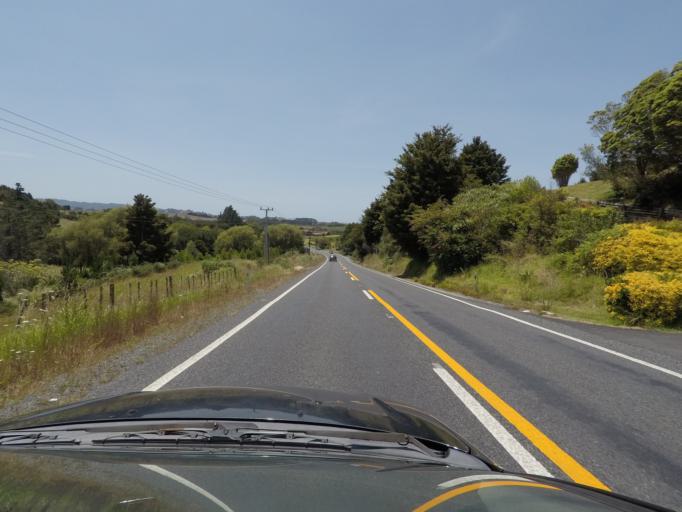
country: NZ
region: Auckland
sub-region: Auckland
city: Warkworth
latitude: -36.3752
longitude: 174.6747
